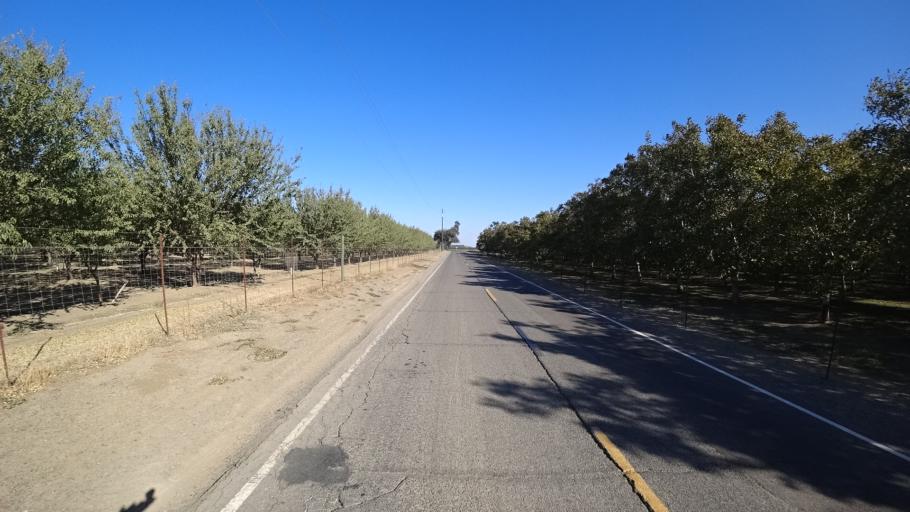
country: US
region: California
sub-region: Yolo County
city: Woodland
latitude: 38.7030
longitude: -121.8626
